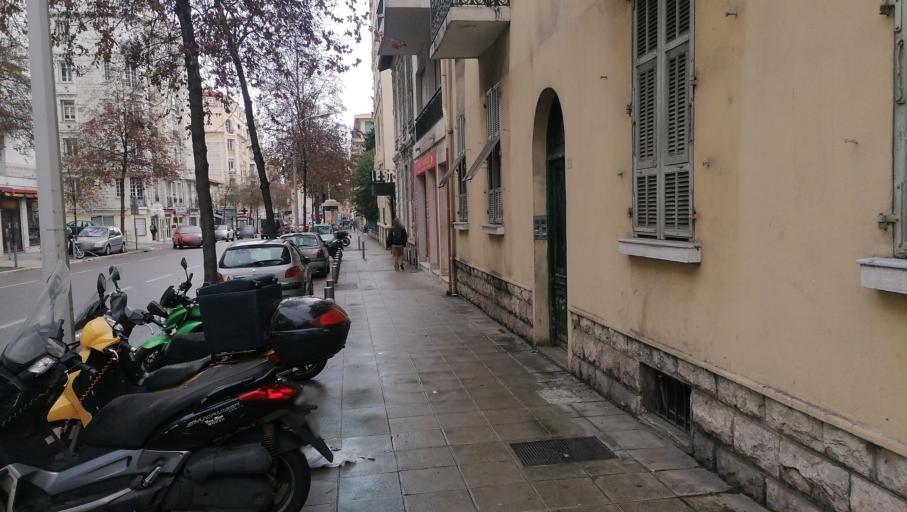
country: FR
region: Provence-Alpes-Cote d'Azur
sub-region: Departement des Alpes-Maritimes
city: Nice
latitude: 43.7117
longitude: 7.2557
